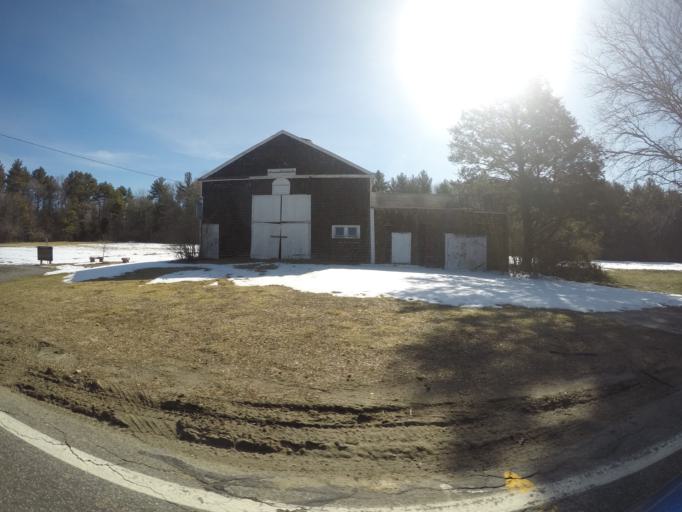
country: US
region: Massachusetts
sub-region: Bristol County
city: Easton
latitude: 42.0052
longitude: -71.1206
